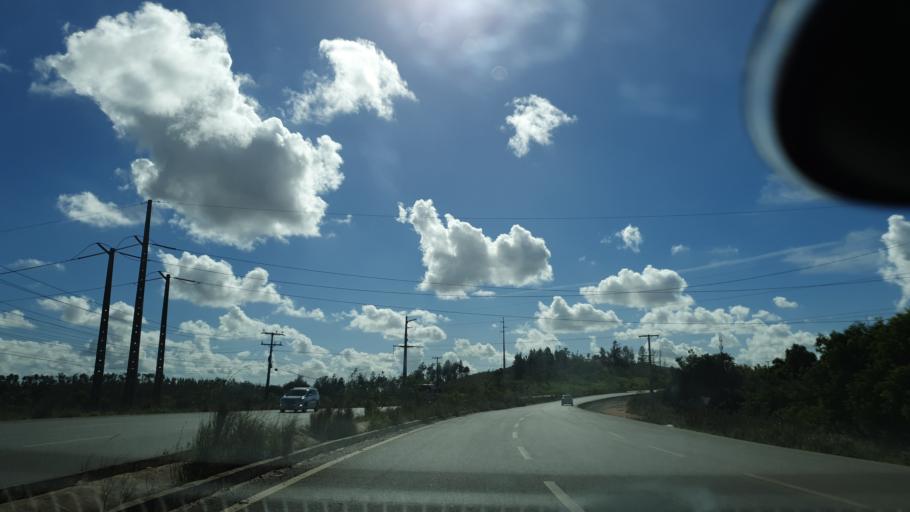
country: BR
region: Bahia
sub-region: Camacari
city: Camacari
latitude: -12.6850
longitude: -38.2707
